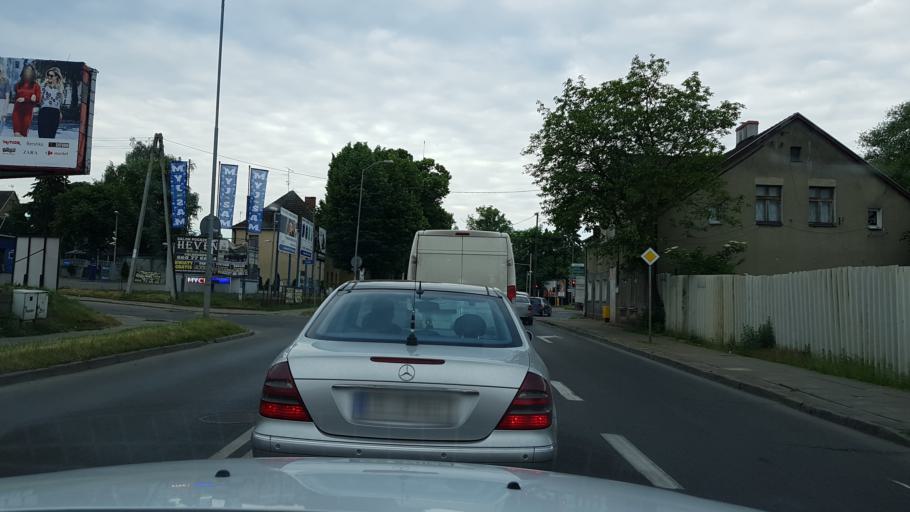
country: PL
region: West Pomeranian Voivodeship
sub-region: Szczecin
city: Szczecin
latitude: 53.3718
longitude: 14.6055
